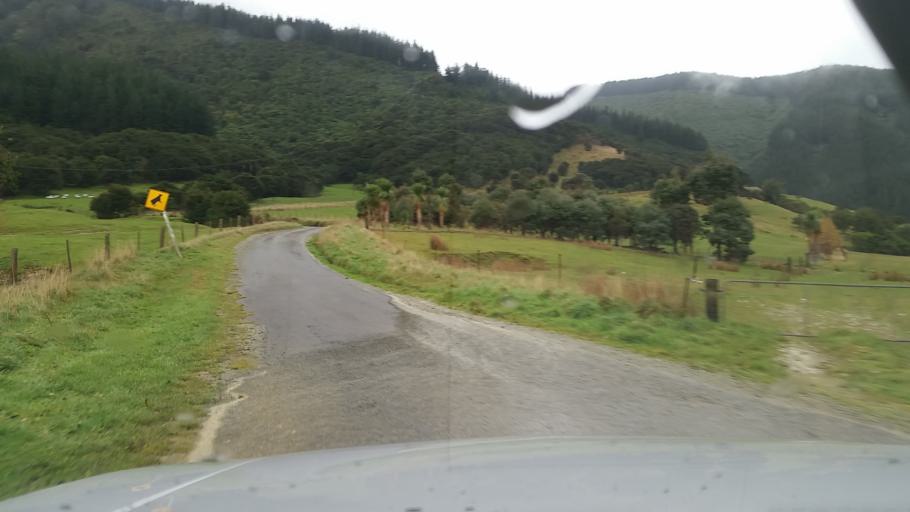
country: NZ
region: Marlborough
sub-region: Marlborough District
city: Picton
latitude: -41.1488
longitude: 174.0518
